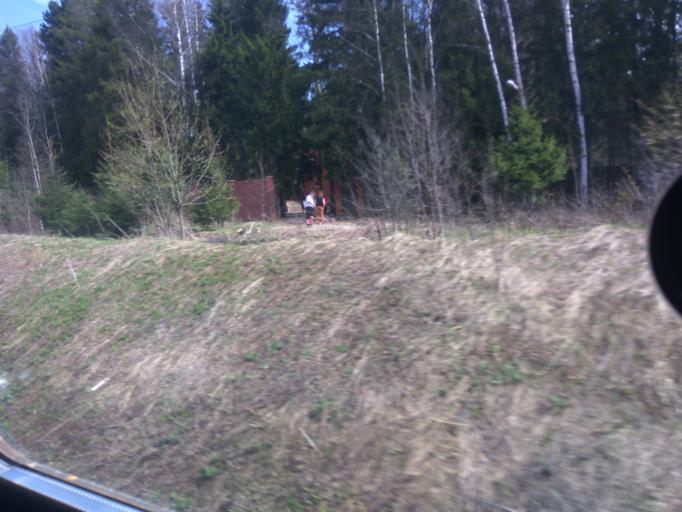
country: RU
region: Moskovskaya
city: Nekrasovskiy
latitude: 56.1124
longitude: 37.5122
